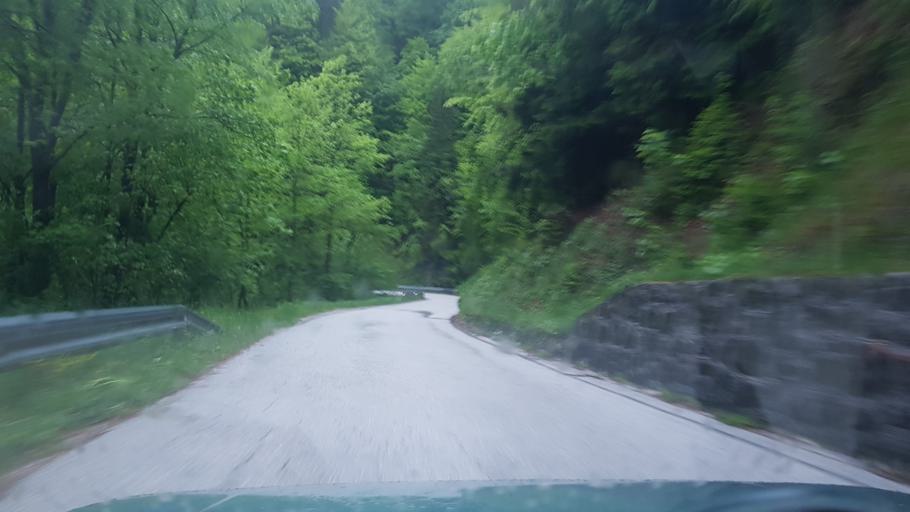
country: SI
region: Bohinj
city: Bohinjska Bistrica
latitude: 46.2214
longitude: 14.0209
